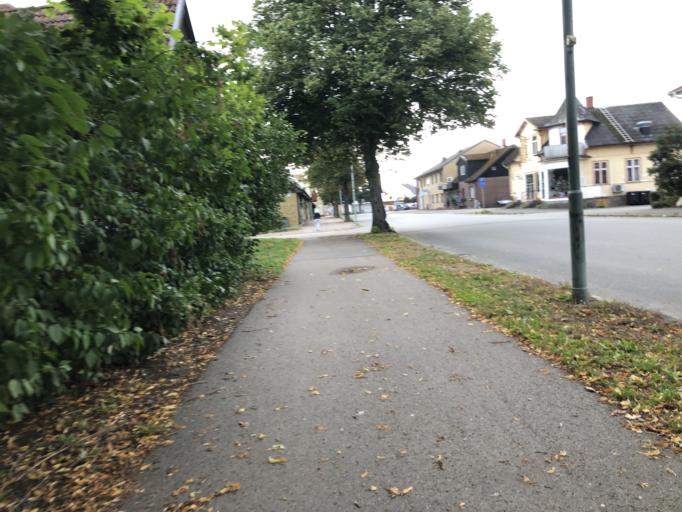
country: SE
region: Skane
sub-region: Hassleholms Kommun
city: Vinslov
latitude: 56.1038
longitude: 13.9137
